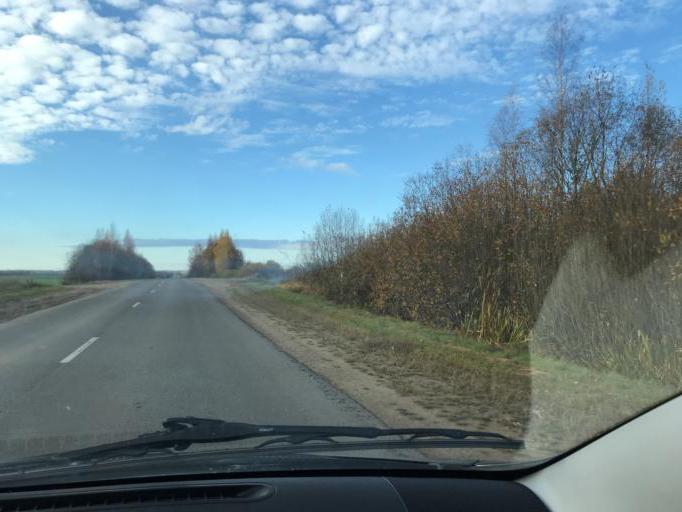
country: BY
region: Vitebsk
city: Haradok
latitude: 55.4156
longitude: 29.7722
